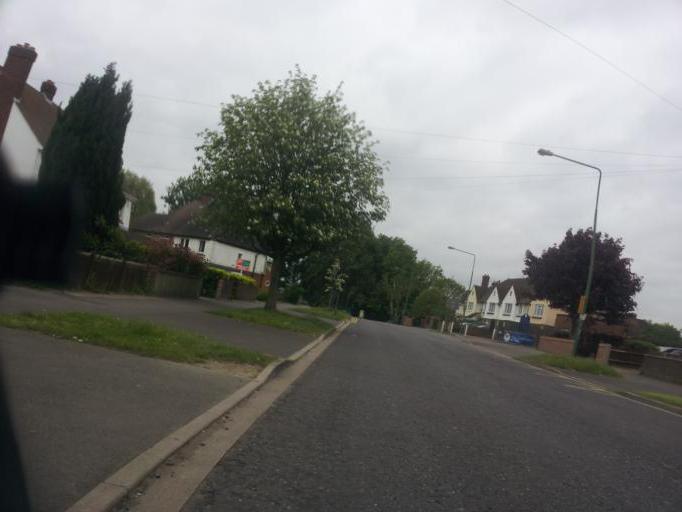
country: GB
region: England
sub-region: Kent
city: Maidstone
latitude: 51.2616
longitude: 0.5336
